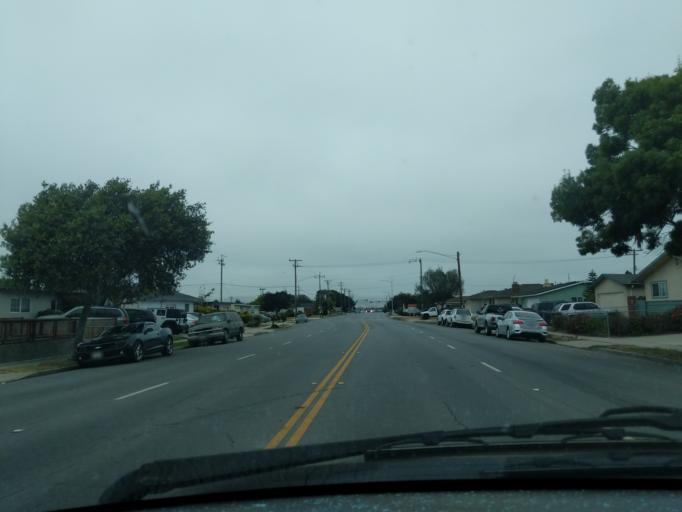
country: US
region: California
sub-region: Monterey County
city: Salinas
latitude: 36.6970
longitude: -121.6419
